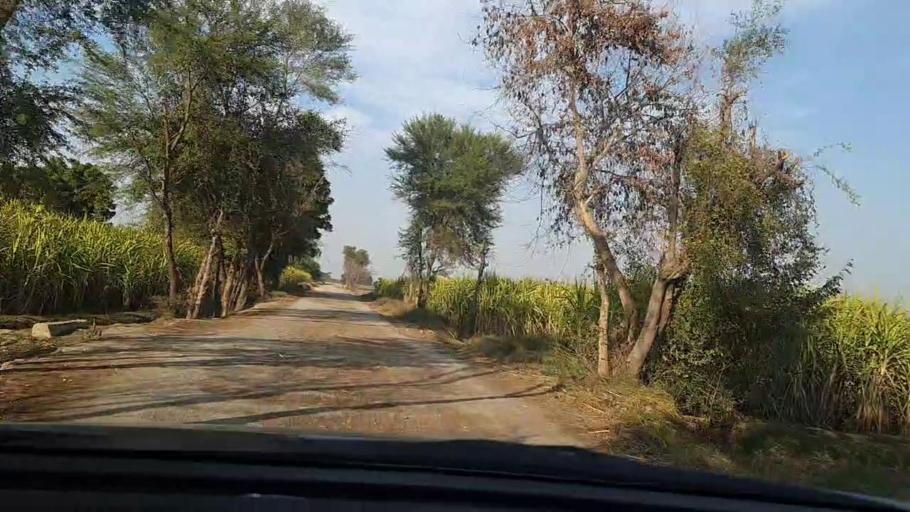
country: PK
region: Sindh
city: Daulatpur
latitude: 26.3328
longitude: 68.0293
